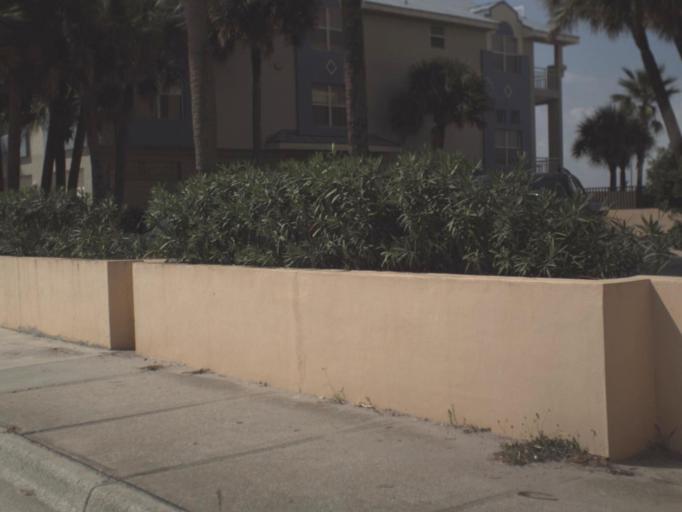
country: US
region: Florida
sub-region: Pinellas County
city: Madeira Beach
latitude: 27.7935
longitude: -82.7919
